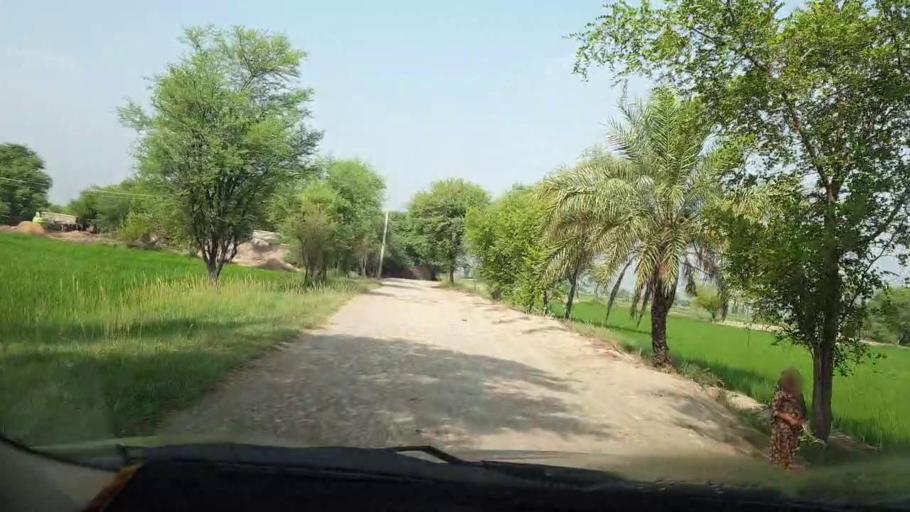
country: PK
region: Sindh
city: Goth Garelo
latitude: 27.4527
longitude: 68.0185
